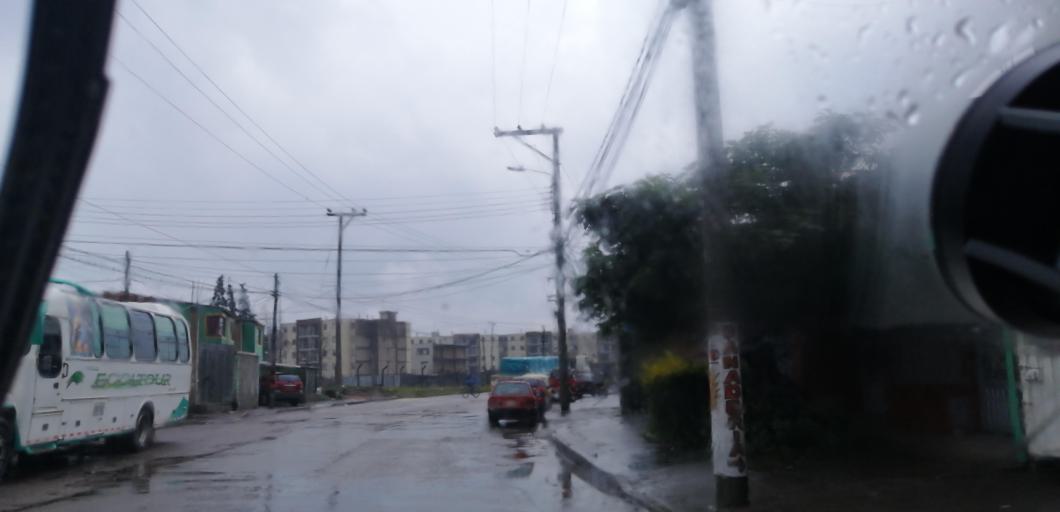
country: CO
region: Cundinamarca
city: Madrid
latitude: 4.7403
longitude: -74.2641
